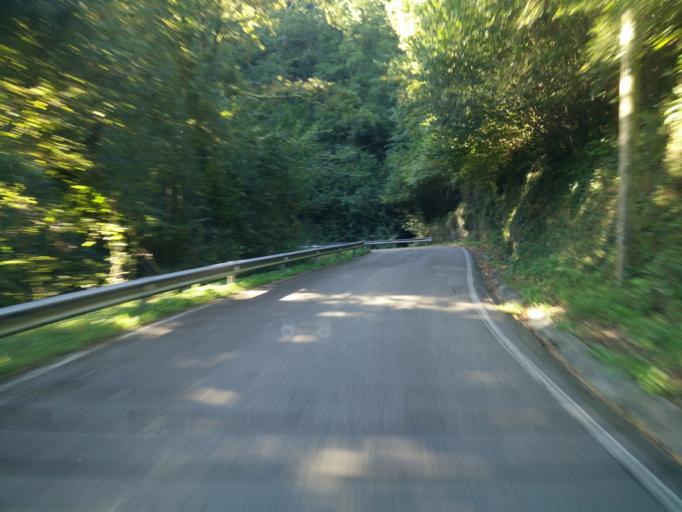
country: ES
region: Cantabria
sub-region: Provincia de Cantabria
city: San Pedro del Romeral
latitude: 43.1420
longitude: -3.8185
